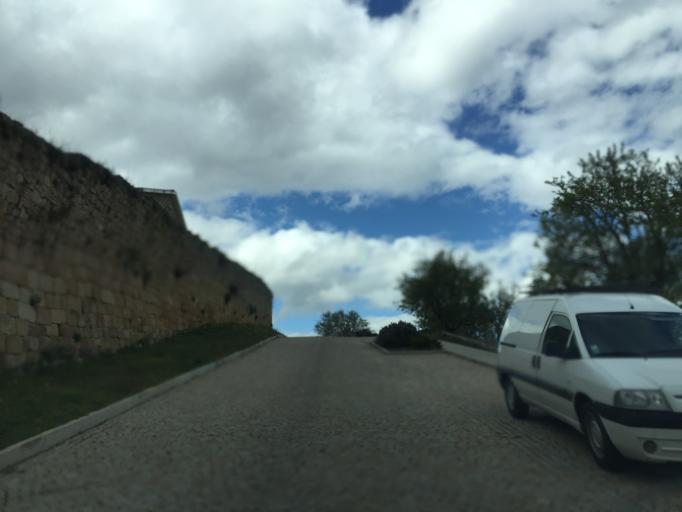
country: PT
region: Braganca
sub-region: Miranda do Douro
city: Miranda do Douro
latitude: 41.4944
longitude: -6.2728
